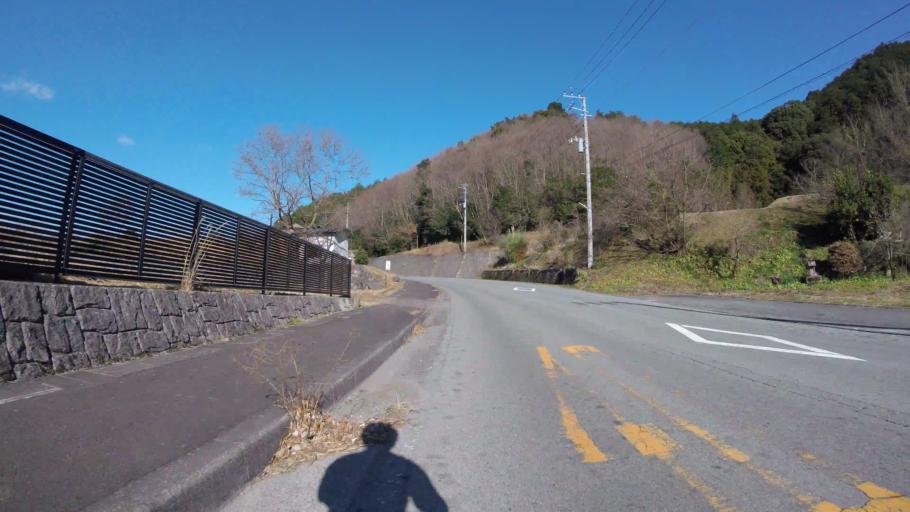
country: JP
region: Shizuoka
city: Ito
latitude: 34.9465
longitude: 138.9973
